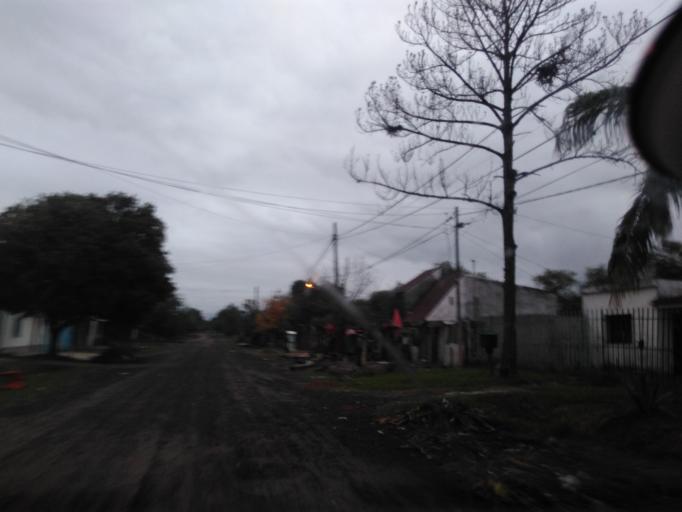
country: AR
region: Chaco
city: Resistencia
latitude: -27.4784
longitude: -58.9921
